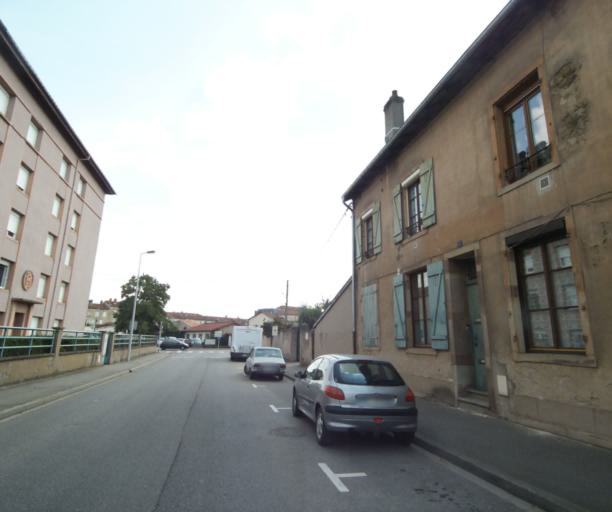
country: FR
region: Lorraine
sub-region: Departement de Meurthe-et-Moselle
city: Luneville
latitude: 48.5903
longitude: 6.4879
